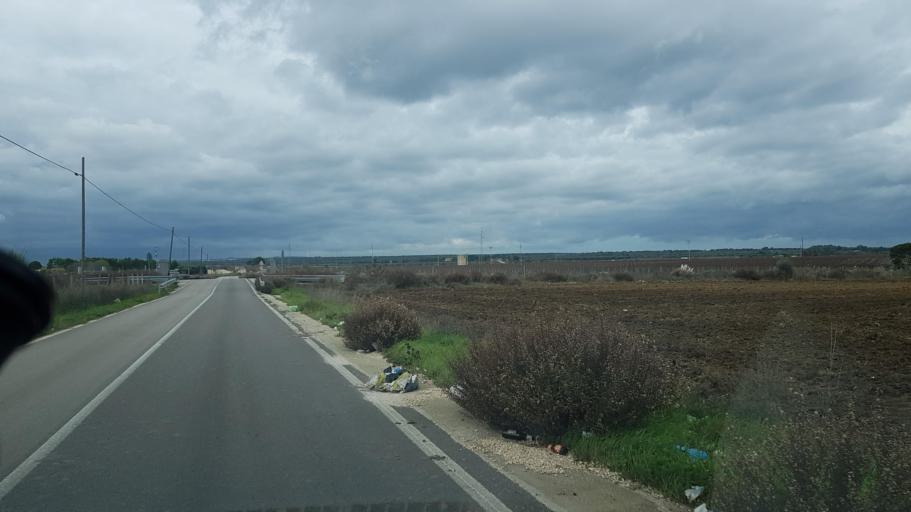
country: IT
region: Apulia
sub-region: Provincia di Brindisi
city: Francavilla Fontana
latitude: 40.5383
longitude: 17.5699
